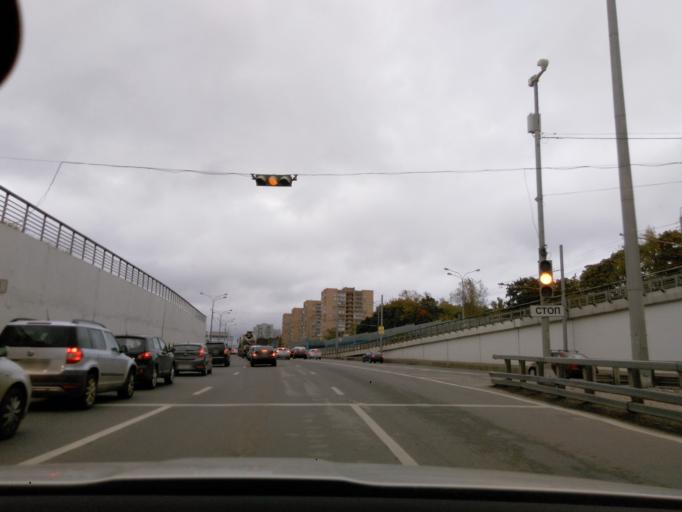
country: RU
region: Moscow
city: Pokrovskoye-Streshnevo
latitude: 55.8187
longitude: 37.4547
